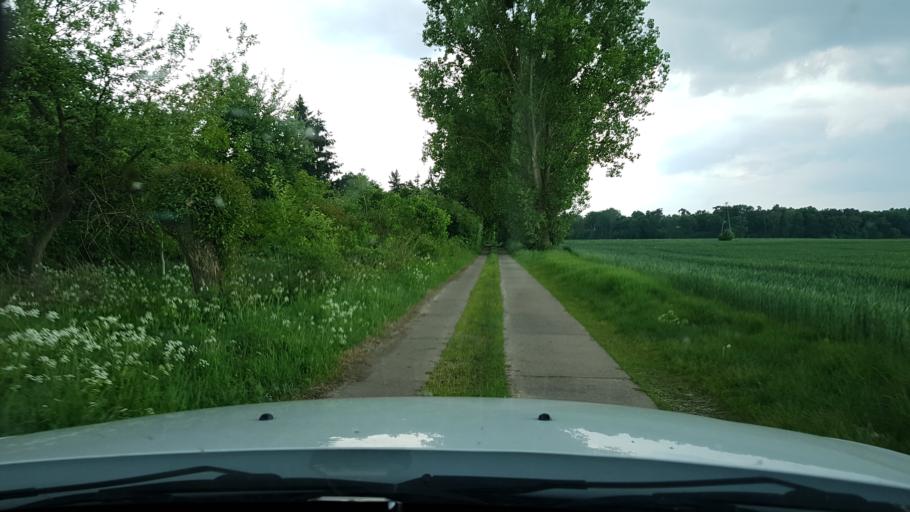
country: PL
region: West Pomeranian Voivodeship
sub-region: Powiat stargardzki
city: Stara Dabrowa
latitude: 53.3524
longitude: 15.1814
